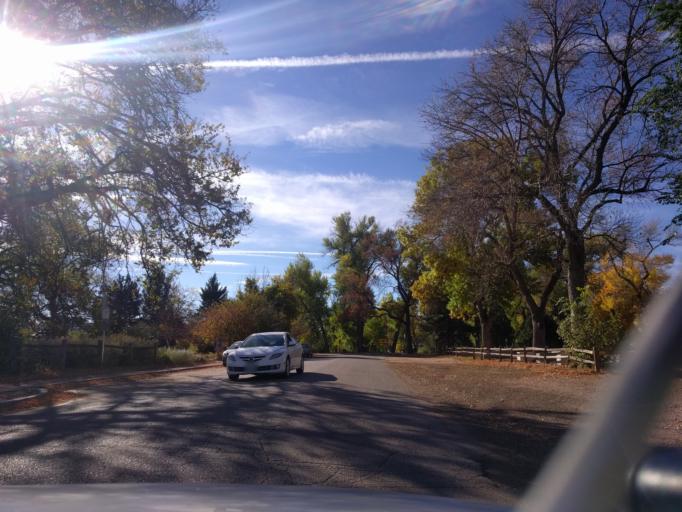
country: US
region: Colorado
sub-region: El Paso County
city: Colorado Springs
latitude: 38.8503
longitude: -104.8299
